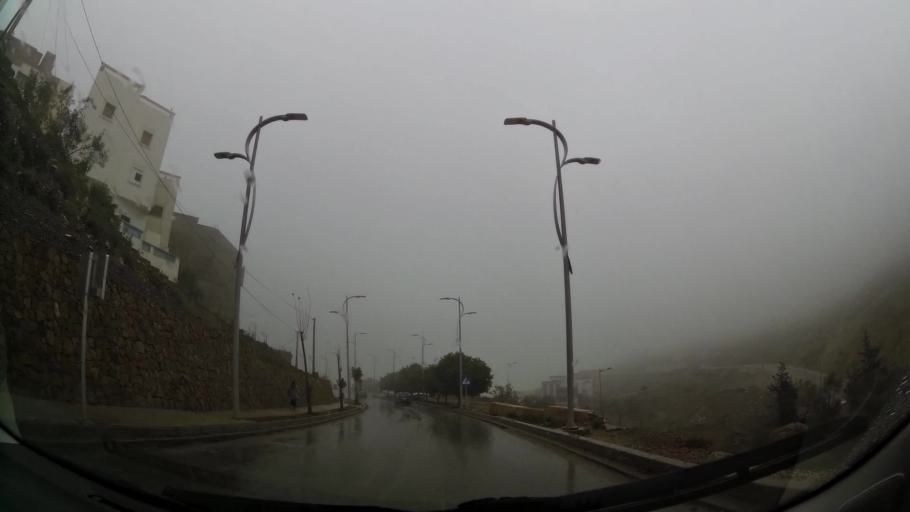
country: MA
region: Taza-Al Hoceima-Taounate
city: Tirhanimine
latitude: 35.2346
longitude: -3.9456
